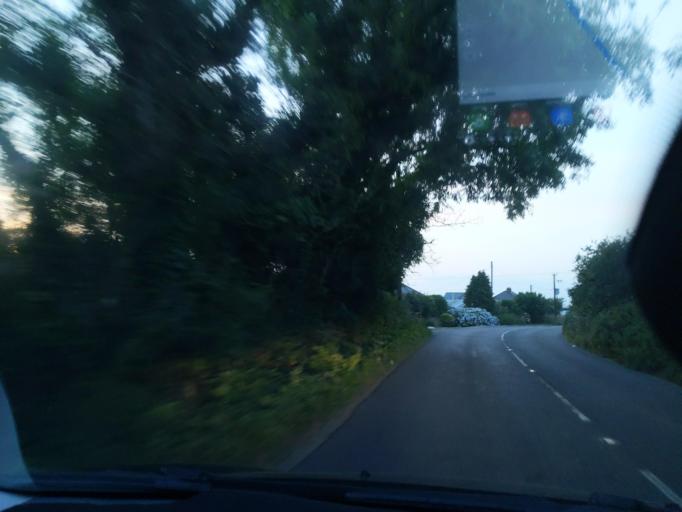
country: GB
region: England
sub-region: Cornwall
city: Camborne
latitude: 50.1802
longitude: -5.3121
